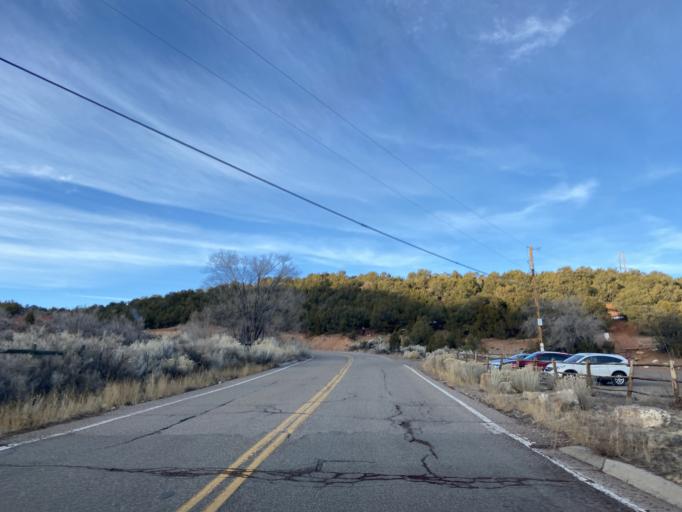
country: US
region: New Mexico
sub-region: Santa Fe County
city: Santa Fe
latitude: 35.7106
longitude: -105.8997
